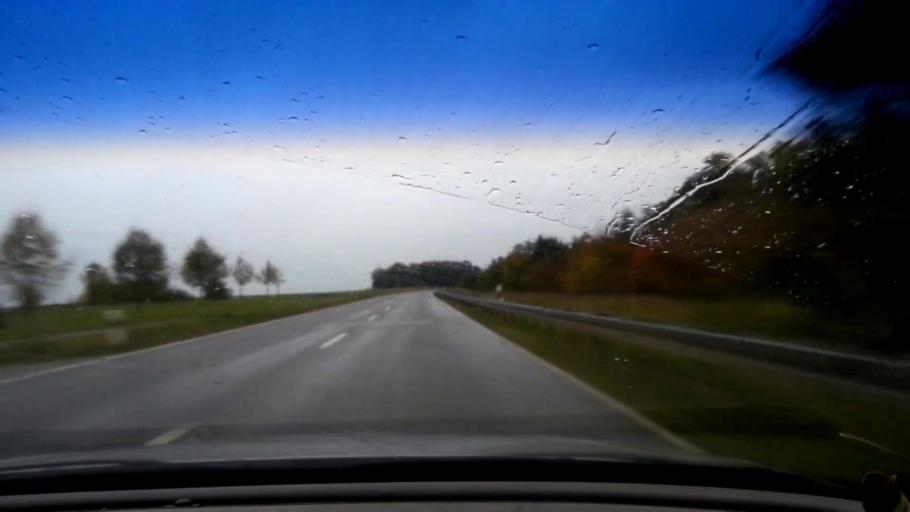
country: DE
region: Bavaria
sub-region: Upper Franconia
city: Walsdorf
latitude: 49.8919
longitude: 10.7779
